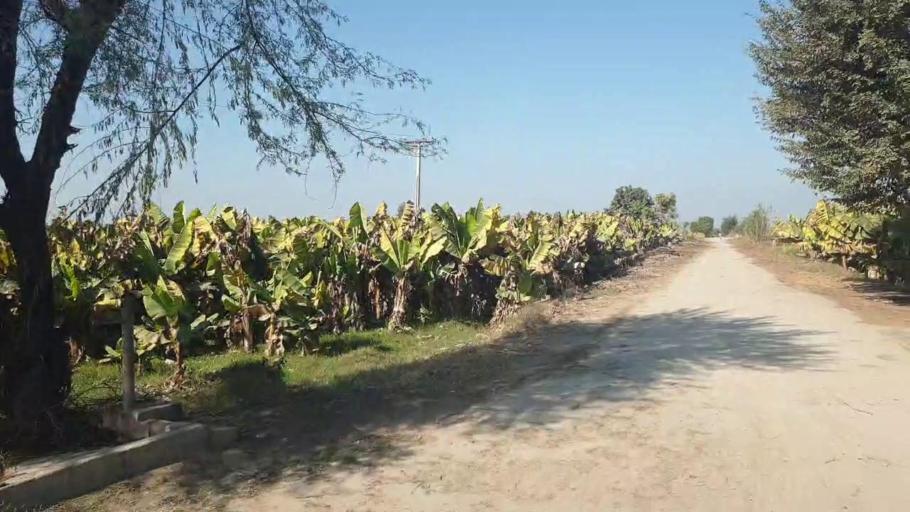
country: PK
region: Sindh
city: Shahdadpur
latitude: 25.9163
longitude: 68.5657
